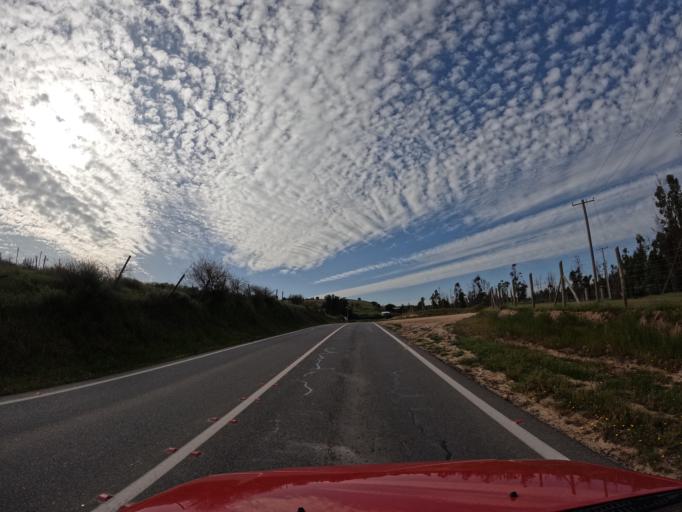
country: CL
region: O'Higgins
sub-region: Provincia de Colchagua
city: Santa Cruz
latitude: -34.2685
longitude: -71.7338
